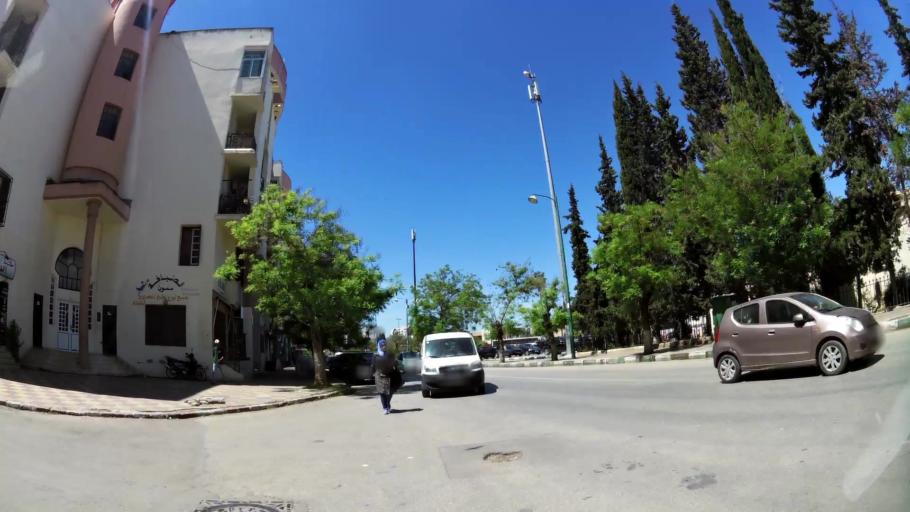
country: MA
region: Meknes-Tafilalet
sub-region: Meknes
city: Meknes
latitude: 33.9034
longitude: -5.5313
